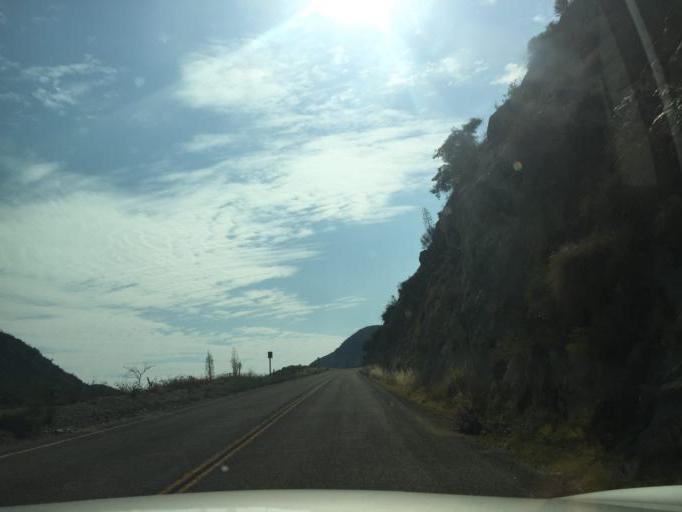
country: US
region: California
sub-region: Los Angeles County
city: Altadena
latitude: 34.2692
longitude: -118.1422
